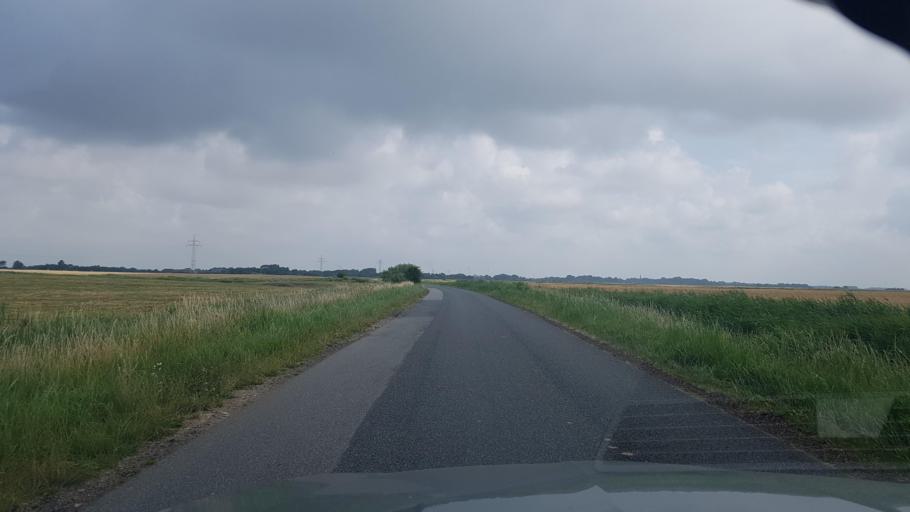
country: DE
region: Schleswig-Holstein
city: Sankt Peter-Ording
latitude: 54.3125
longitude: 8.6618
